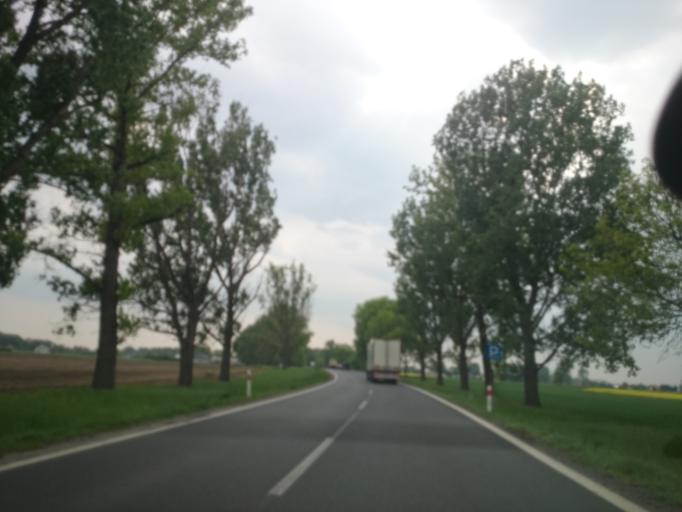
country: PL
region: Lower Silesian Voivodeship
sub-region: Powiat wroclawski
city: Kobierzyce
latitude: 50.9459
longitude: 16.9049
